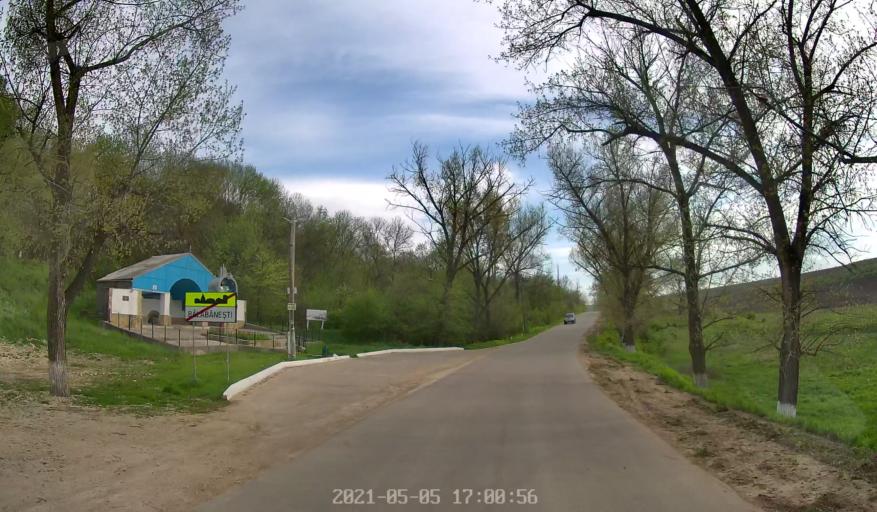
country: MD
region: Chisinau
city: Vadul lui Voda
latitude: 47.0618
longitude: 29.1337
